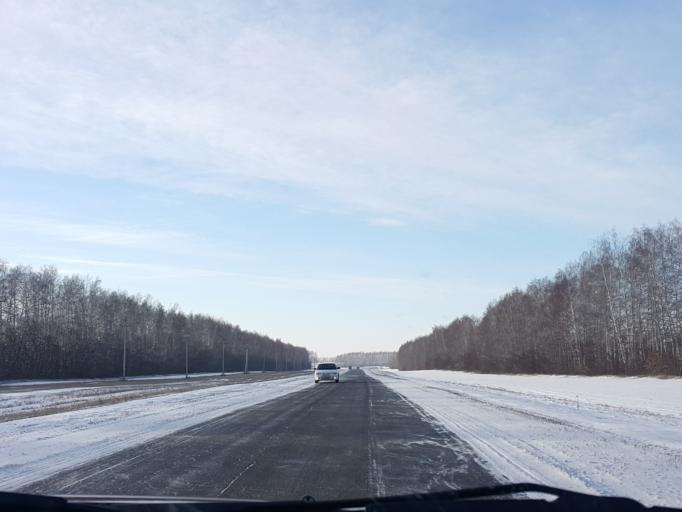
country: RU
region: Tambov
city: Znamenka
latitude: 52.3779
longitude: 41.3128
